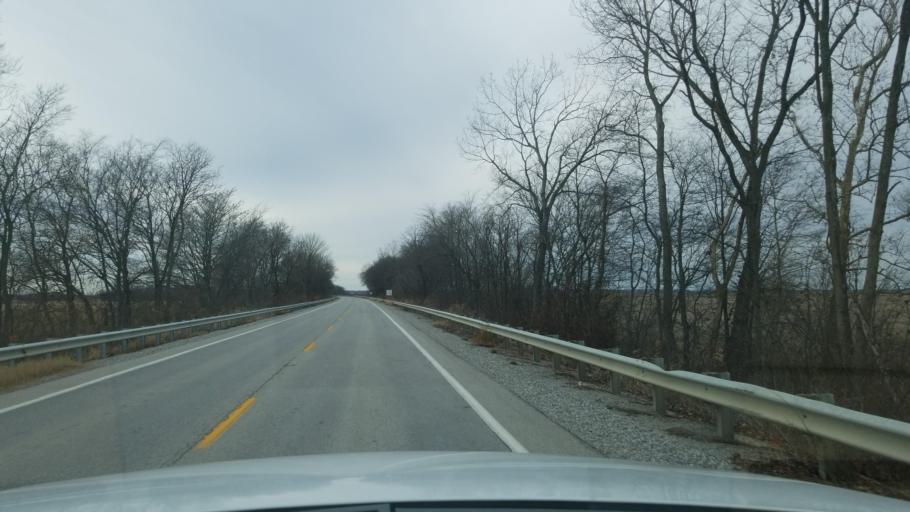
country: US
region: Indiana
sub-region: Posey County
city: Mount Vernon
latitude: 37.9435
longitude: -88.0473
